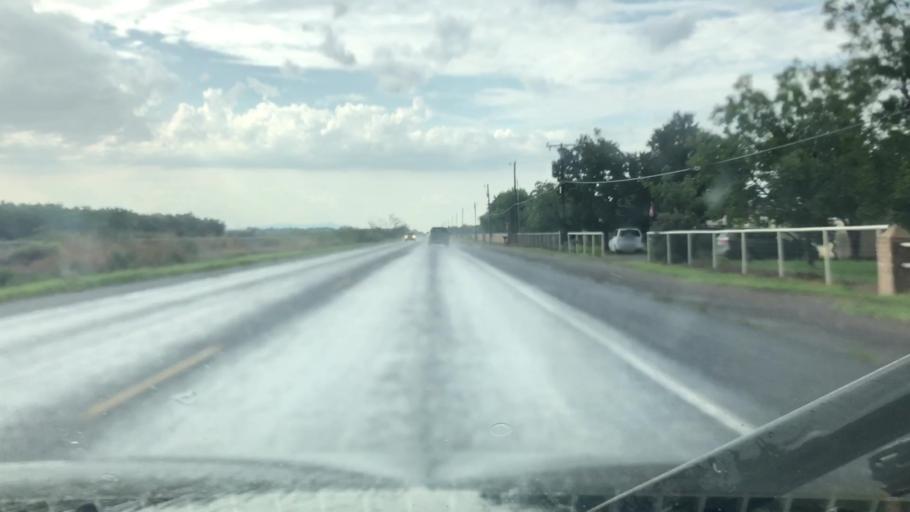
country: US
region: New Mexico
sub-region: Dona Ana County
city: Mesquite
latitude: 32.1814
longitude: -106.7071
